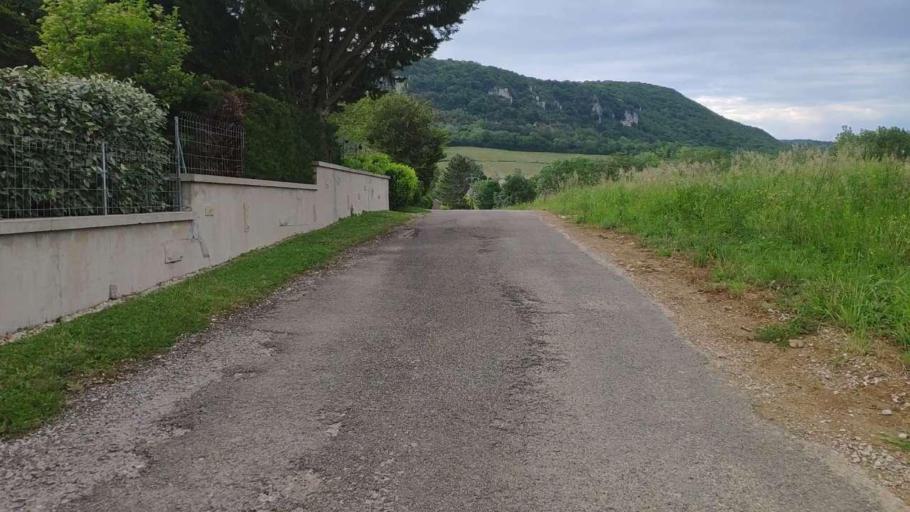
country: FR
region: Franche-Comte
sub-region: Departement du Jura
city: Perrigny
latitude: 46.7162
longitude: 5.5902
